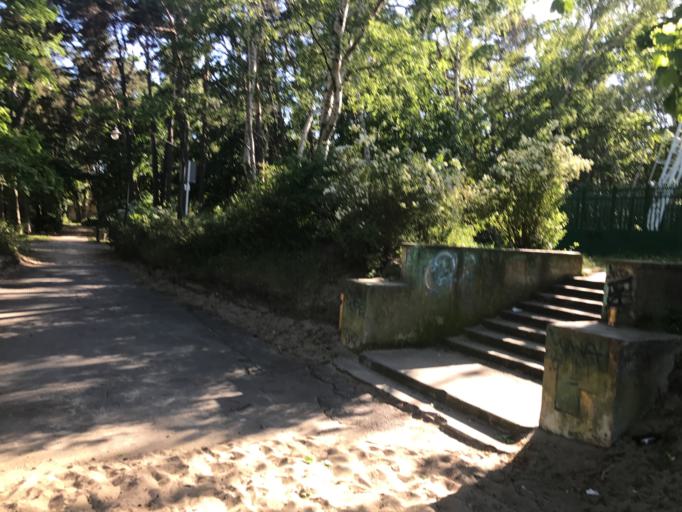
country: PL
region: Pomeranian Voivodeship
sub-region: Gdansk
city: Gdansk
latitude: 54.4087
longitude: 18.6406
